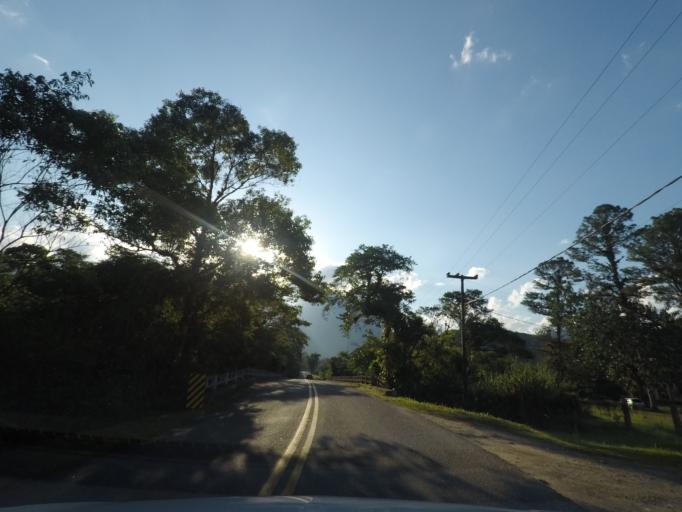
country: BR
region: Parana
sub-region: Antonina
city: Antonina
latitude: -25.3817
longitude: -48.8639
